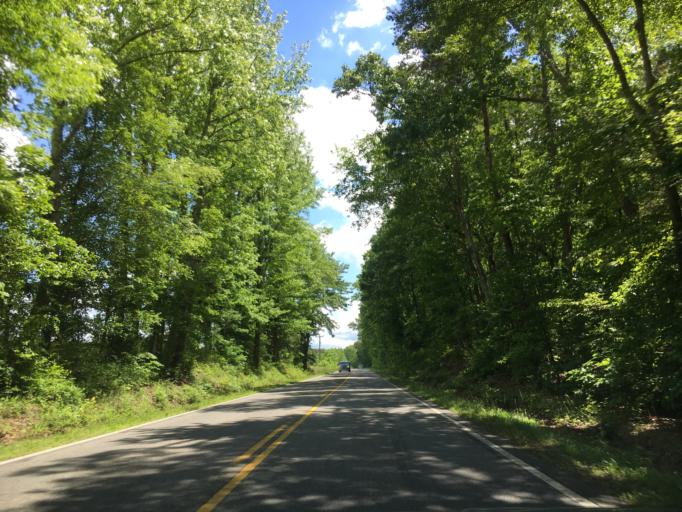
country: US
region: Virginia
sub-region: Halifax County
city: South Boston
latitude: 36.7191
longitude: -78.9419
